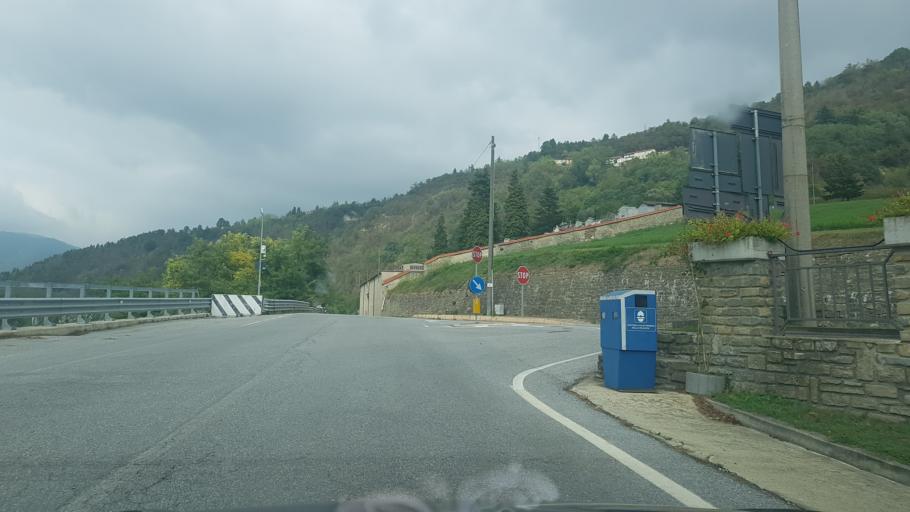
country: IT
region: Piedmont
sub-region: Provincia di Cuneo
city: Monesiglio
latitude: 44.4674
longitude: 8.1162
